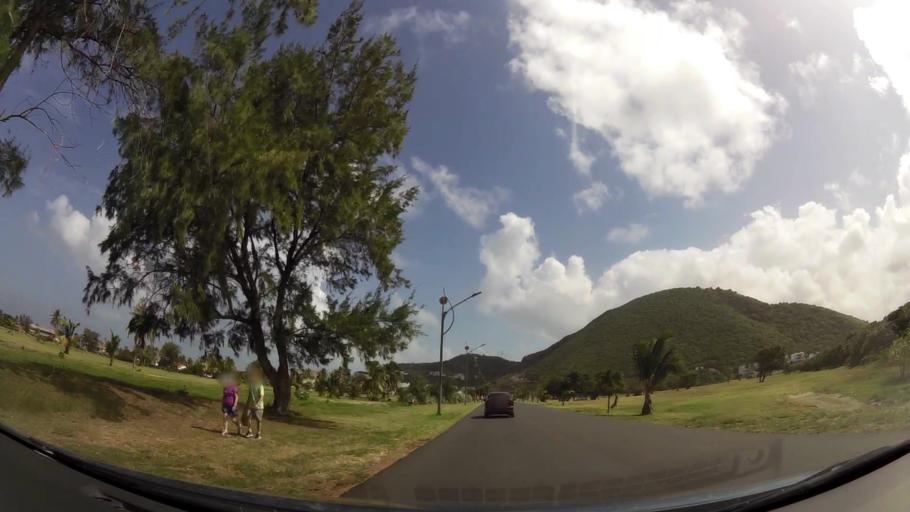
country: KN
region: Saint George Basseterre
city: Basseterre
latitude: 17.2847
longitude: -62.6881
